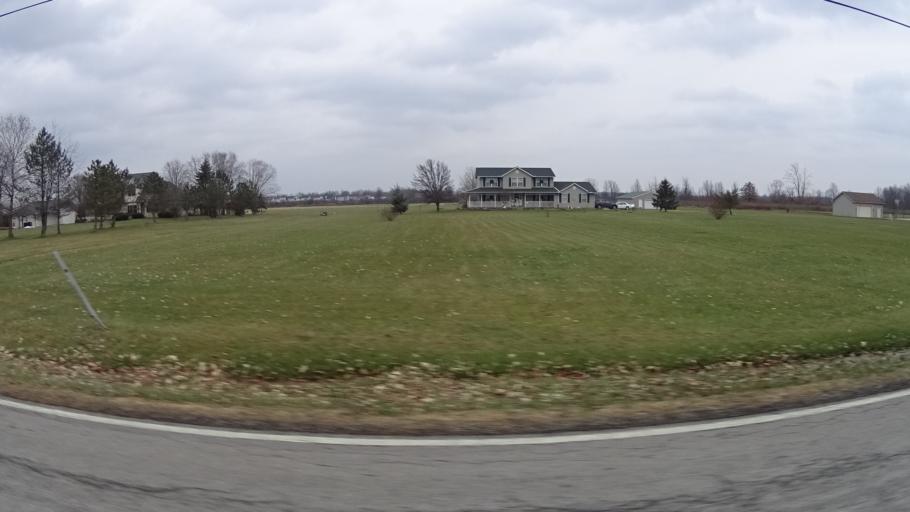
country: US
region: Ohio
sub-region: Lorain County
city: Amherst
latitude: 41.3617
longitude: -82.1754
